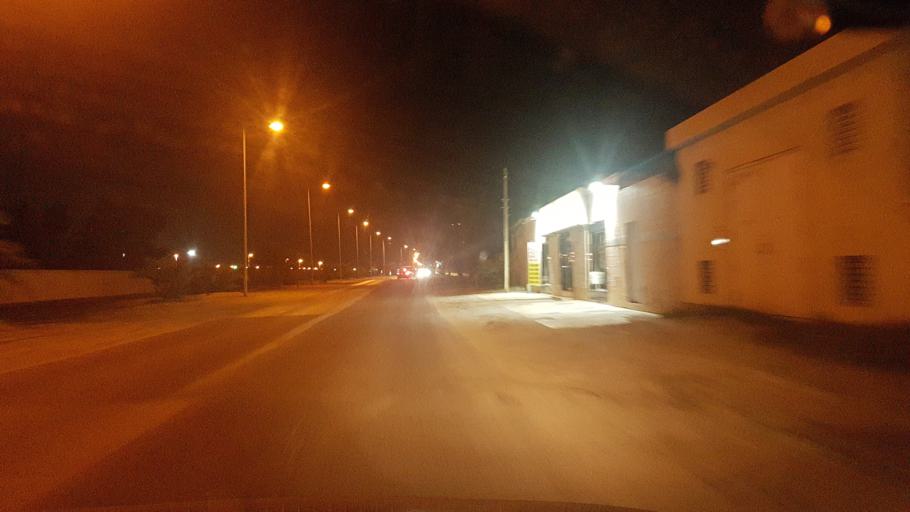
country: BH
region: Muharraq
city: Al Hadd
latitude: 26.2751
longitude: 50.6412
